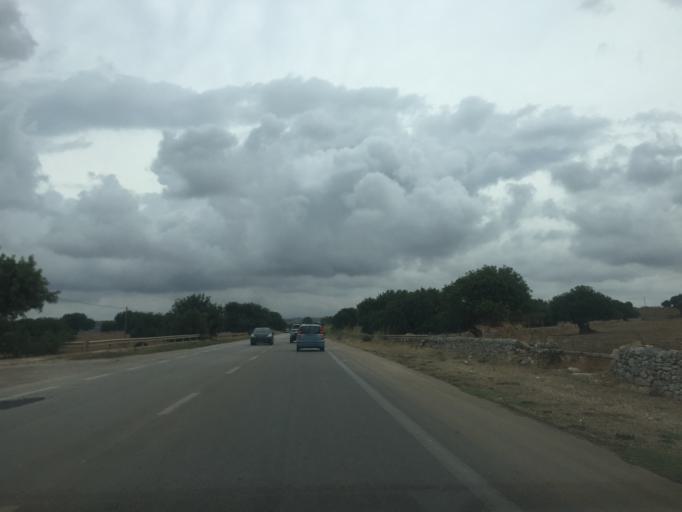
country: IT
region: Sicily
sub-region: Ragusa
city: Marina di Ragusa
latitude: 36.8253
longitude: 14.5829
